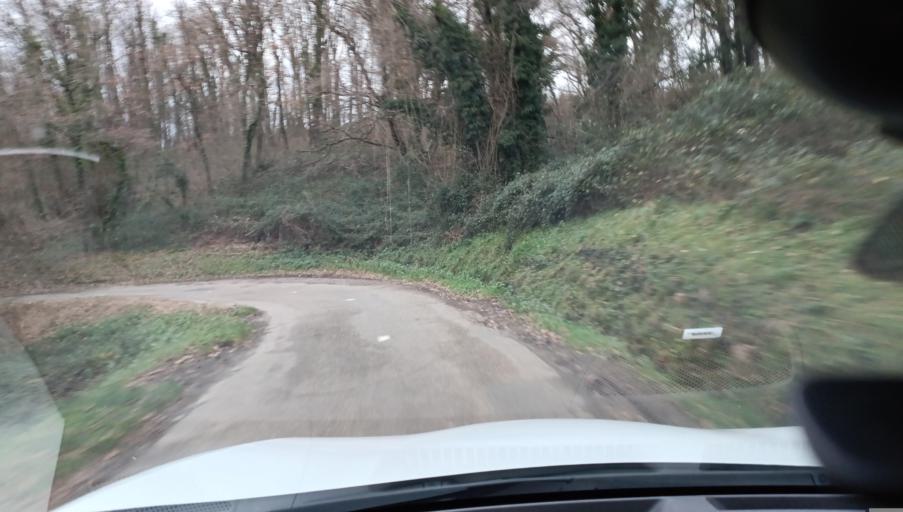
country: FR
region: Rhone-Alpes
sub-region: Departement de l'Isere
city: Chasse-sur-Rhone
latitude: 45.5758
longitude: 4.8224
